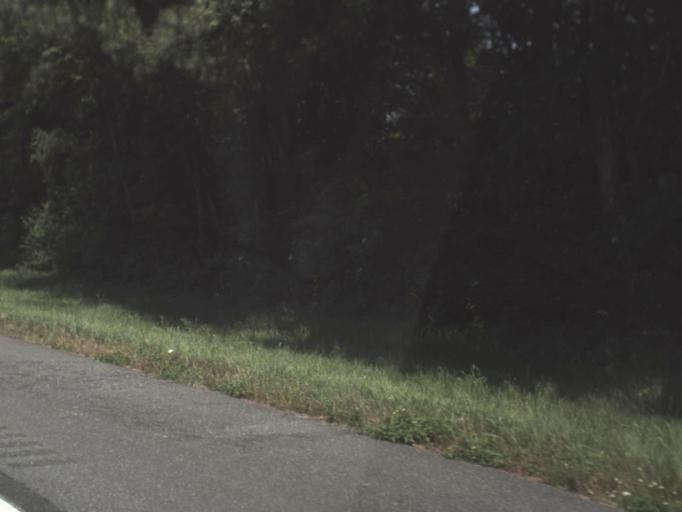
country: US
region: Florida
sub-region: Baker County
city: Macclenny
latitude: 30.2580
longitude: -82.1850
